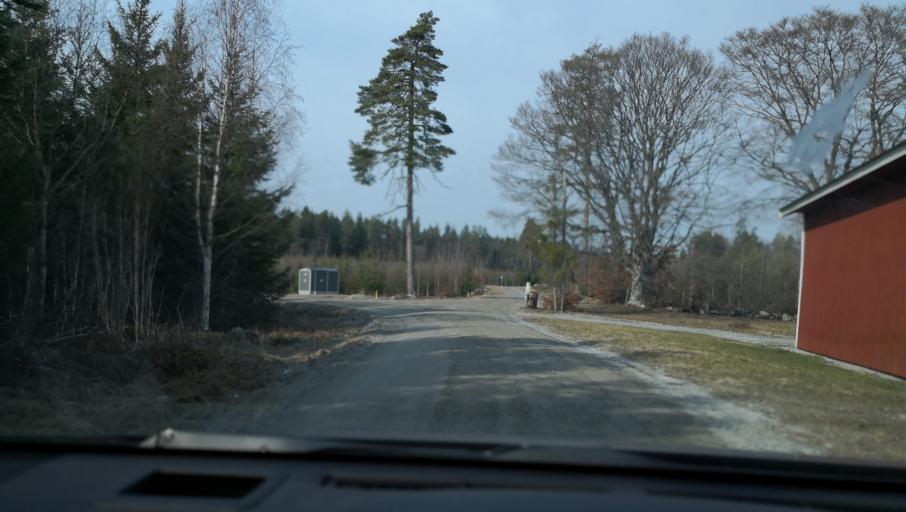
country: SE
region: OErebro
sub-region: Lindesbergs Kommun
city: Frovi
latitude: 59.3633
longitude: 15.4329
